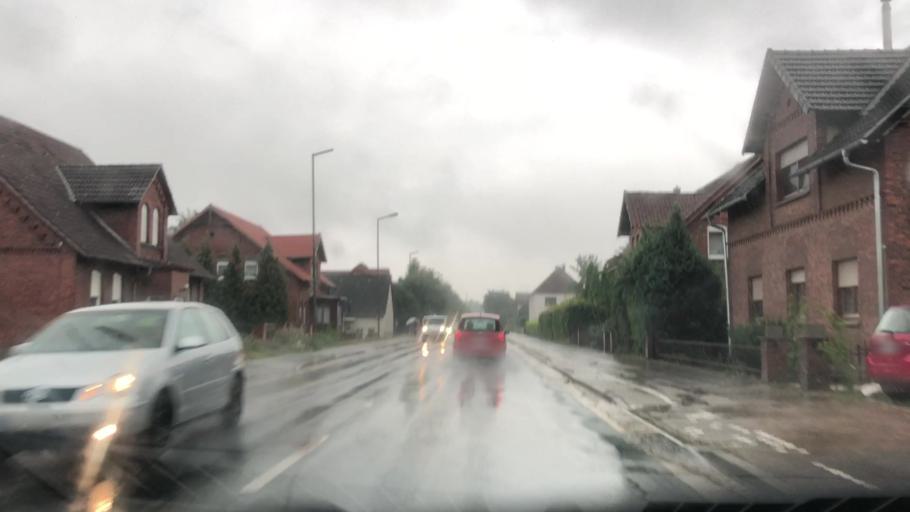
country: DE
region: North Rhine-Westphalia
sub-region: Regierungsbezirk Detmold
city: Minden
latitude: 52.2835
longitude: 8.9518
